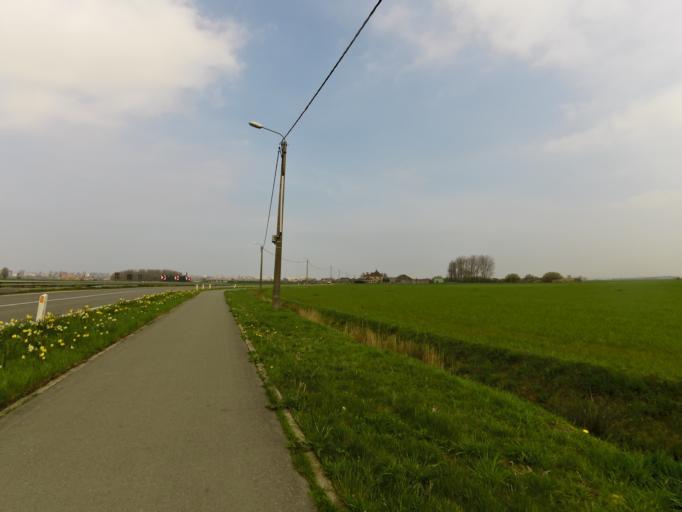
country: BE
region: Flanders
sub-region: Provincie West-Vlaanderen
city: Middelkerke
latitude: 51.1686
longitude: 2.8284
